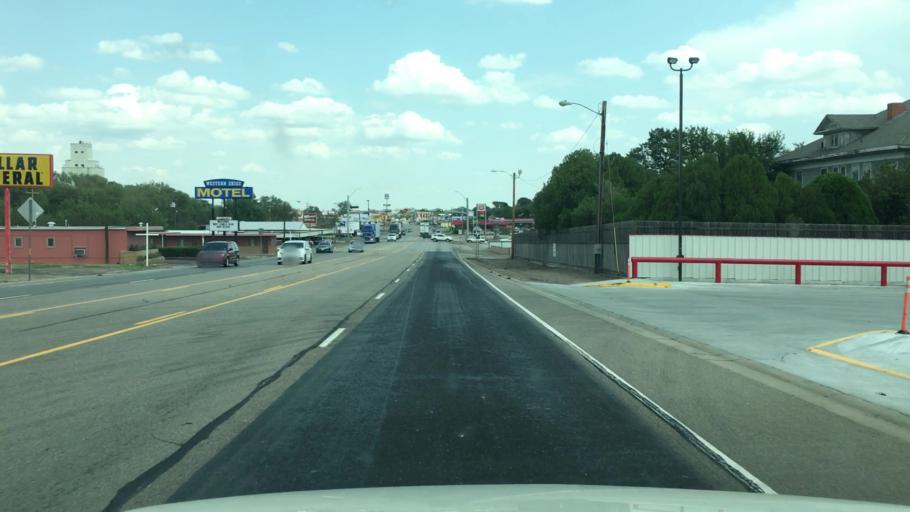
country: US
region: Texas
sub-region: Donley County
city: Clarendon
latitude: 34.9419
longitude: -100.8963
